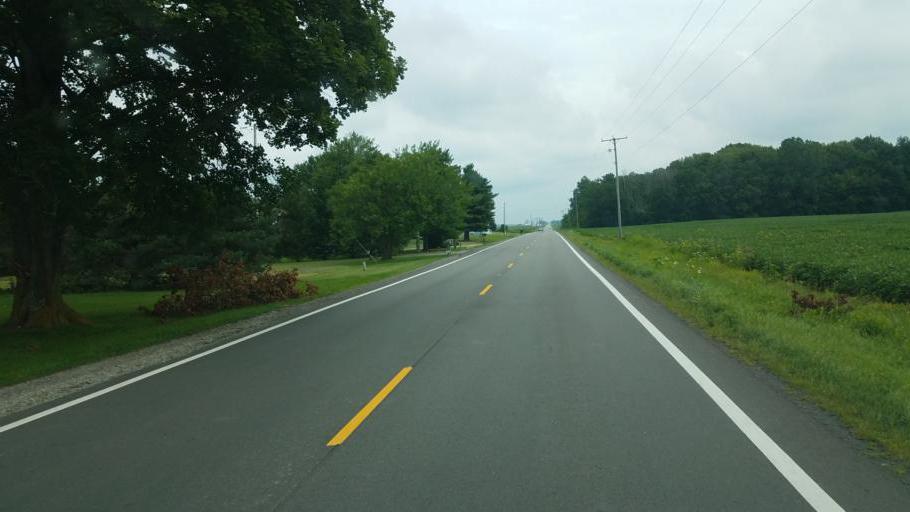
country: US
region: Ohio
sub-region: Crawford County
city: Bucyrus
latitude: 40.6972
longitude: -83.0061
